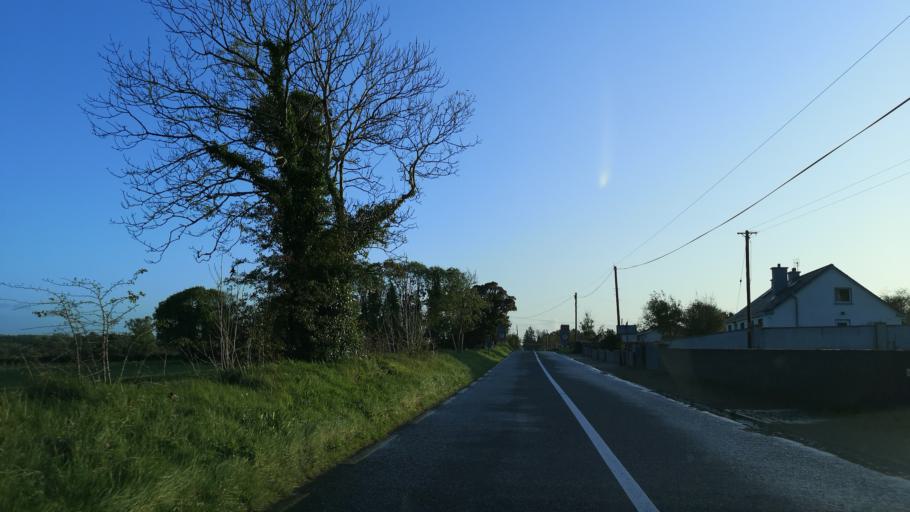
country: IE
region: Connaught
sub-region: Roscommon
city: Castlerea
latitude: 53.7316
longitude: -8.5534
